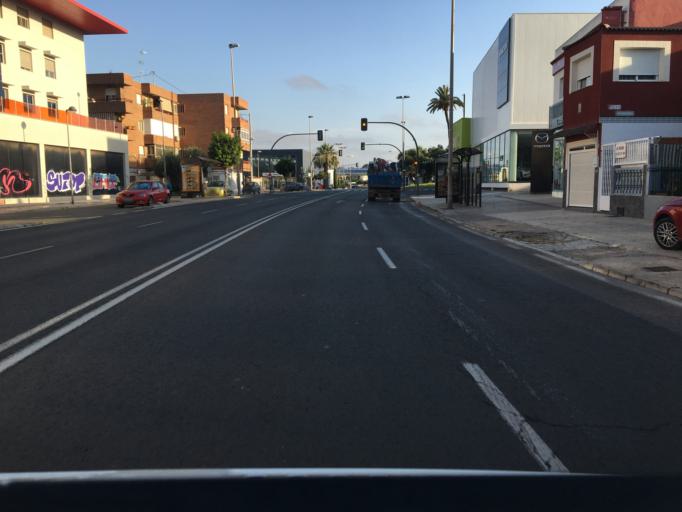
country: ES
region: Murcia
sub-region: Murcia
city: Cartagena
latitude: 37.6261
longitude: -1.0015
